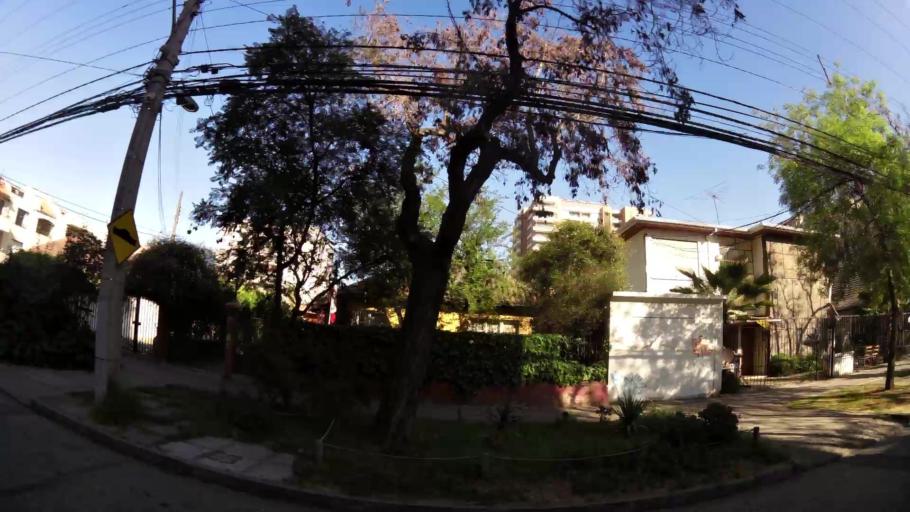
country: CL
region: Santiago Metropolitan
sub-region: Provincia de Santiago
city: Villa Presidente Frei, Nunoa, Santiago, Chile
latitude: -33.4496
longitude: -70.5915
